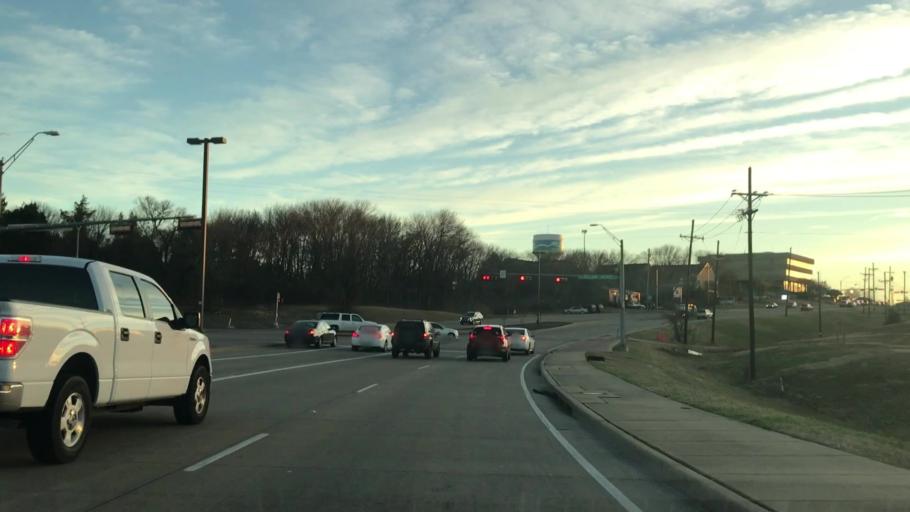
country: US
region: Texas
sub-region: Rockwall County
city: Rockwall
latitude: 32.9050
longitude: -96.4635
